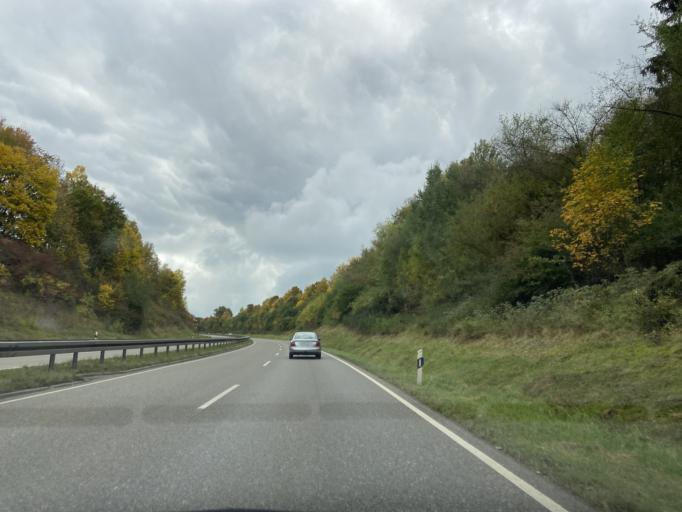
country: DE
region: Baden-Wuerttemberg
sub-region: Tuebingen Region
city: Sigmaringen
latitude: 48.0732
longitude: 9.2097
